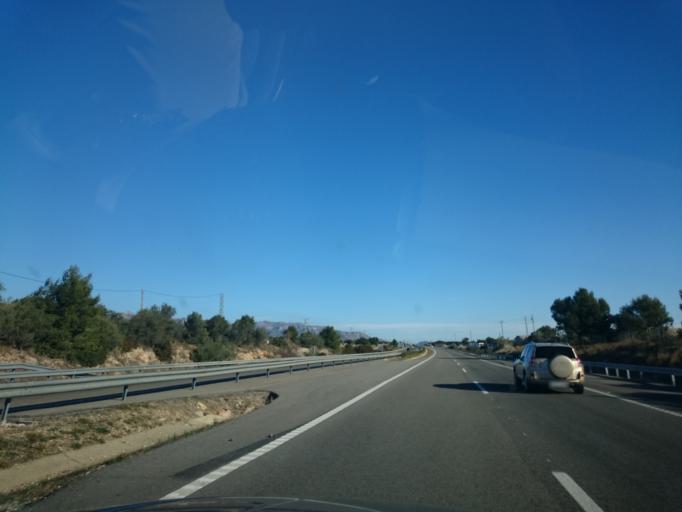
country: ES
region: Catalonia
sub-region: Provincia de Tarragona
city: l'Ametlla de Mar
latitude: 40.8876
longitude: 0.8003
